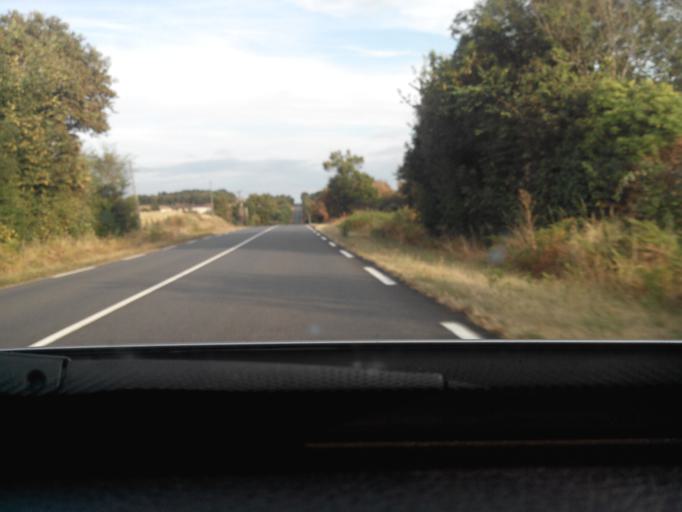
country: FR
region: Poitou-Charentes
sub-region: Departement de la Charente
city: Etagnac
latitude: 45.9085
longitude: 0.7563
